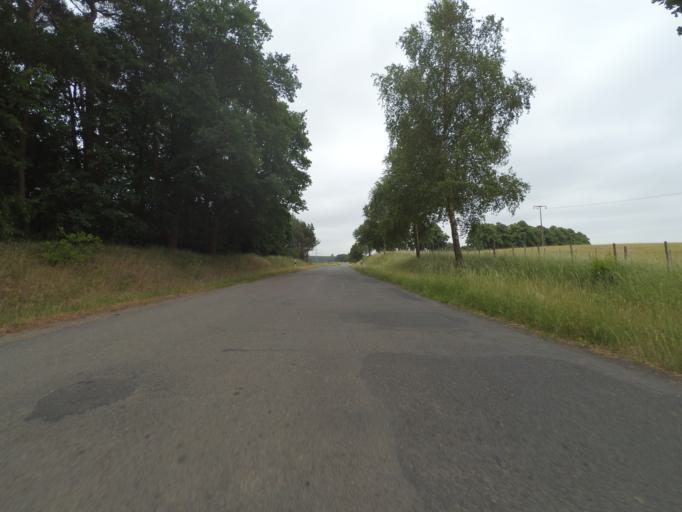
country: DE
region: Mecklenburg-Vorpommern
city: Sternberg
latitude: 53.6575
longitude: 11.8153
